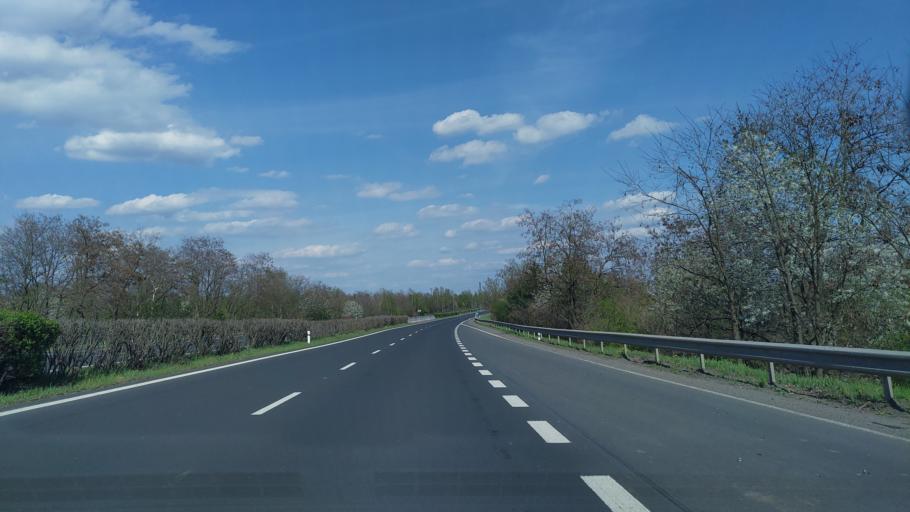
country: CZ
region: Ustecky
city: Horni Jiretin
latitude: 50.5234
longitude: 13.5463
